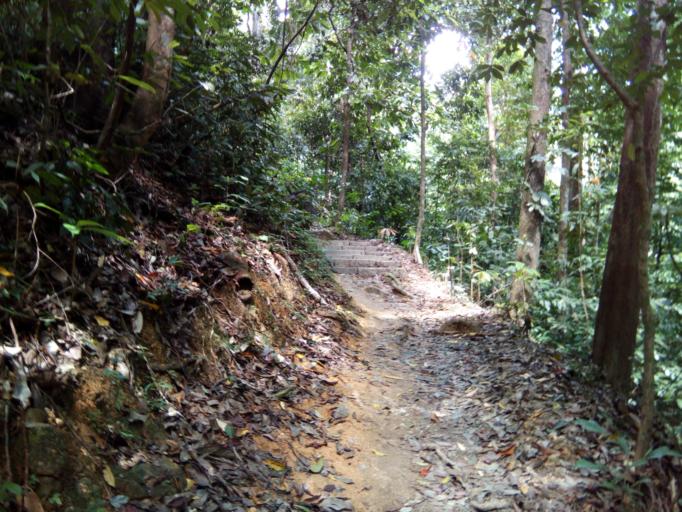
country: MY
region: Penang
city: Tanjung Tokong
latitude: 5.4393
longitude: 100.2861
